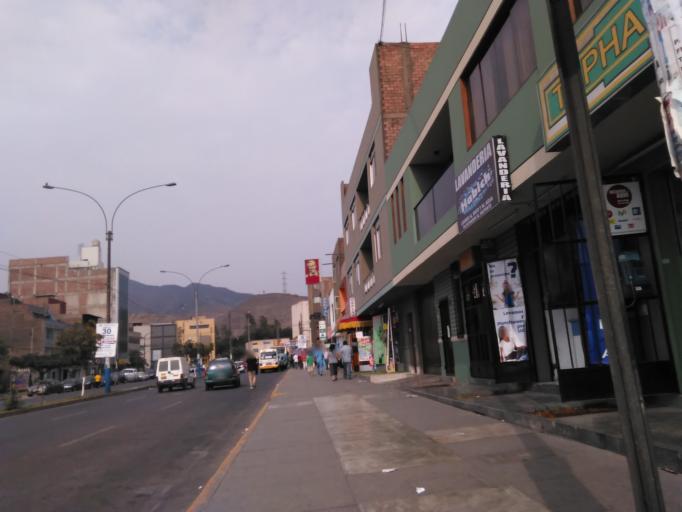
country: PE
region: Lima
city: Lima
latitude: -12.0242
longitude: -77.0511
